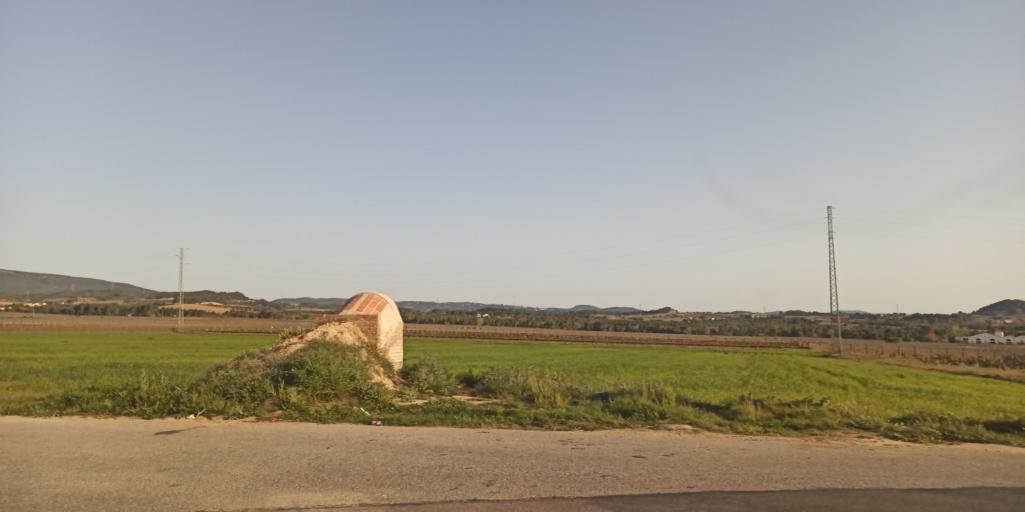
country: ES
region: Catalonia
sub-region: Provincia de Barcelona
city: el Pla del Penedes
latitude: 41.4182
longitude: 1.6971
